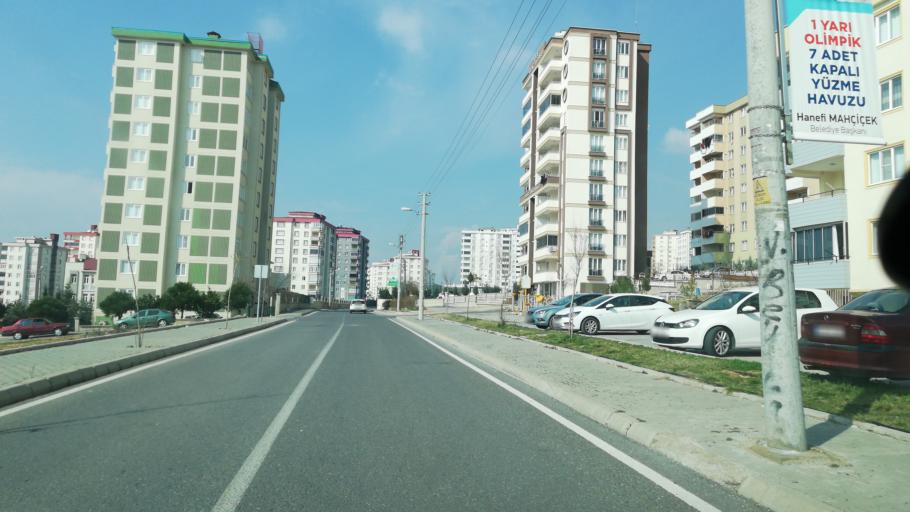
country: TR
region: Kahramanmaras
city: Kahramanmaras
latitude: 37.5893
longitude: 36.8618
